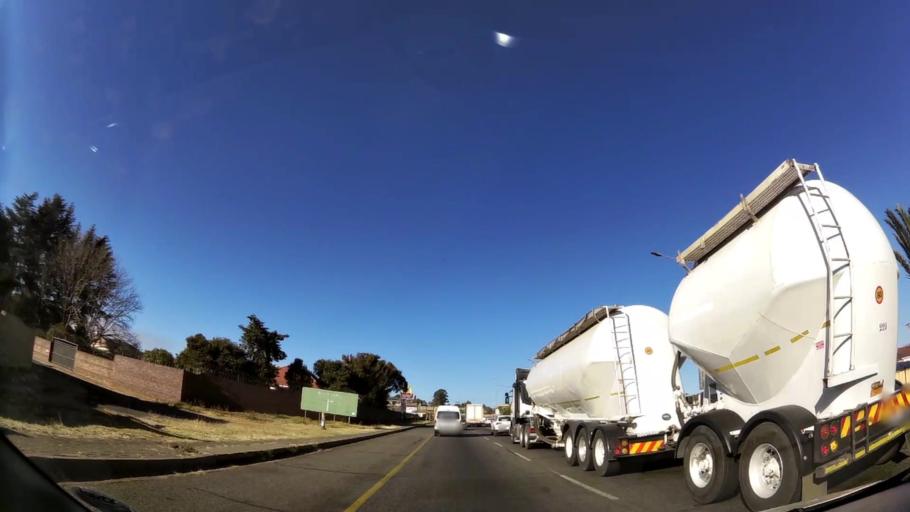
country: ZA
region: Gauteng
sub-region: West Rand District Municipality
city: Krugersdorp
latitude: -26.1058
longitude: 27.7788
